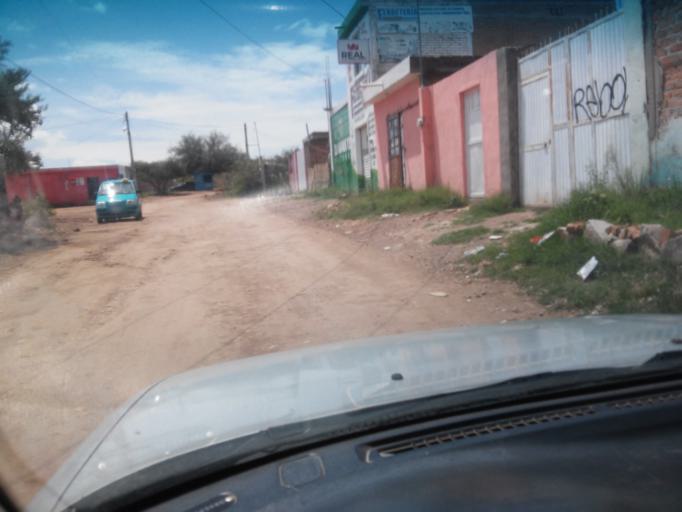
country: MX
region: Durango
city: Victoria de Durango
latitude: 23.9847
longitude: -104.7102
